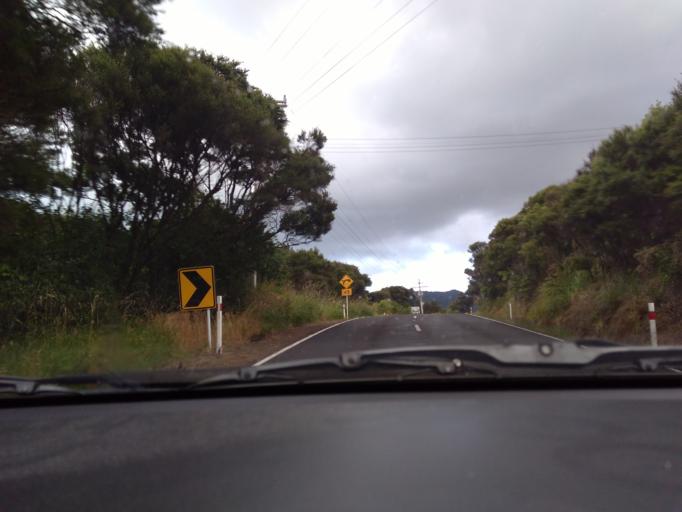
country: NZ
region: Auckland
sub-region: Auckland
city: Titirangi
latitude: -37.0071
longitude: 174.5804
